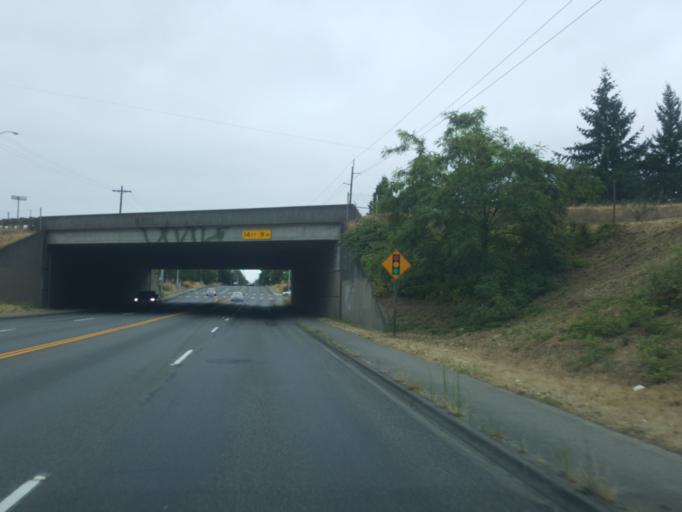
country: US
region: Washington
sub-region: Pierce County
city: McChord Air Force Base
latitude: 47.1702
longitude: -122.4740
